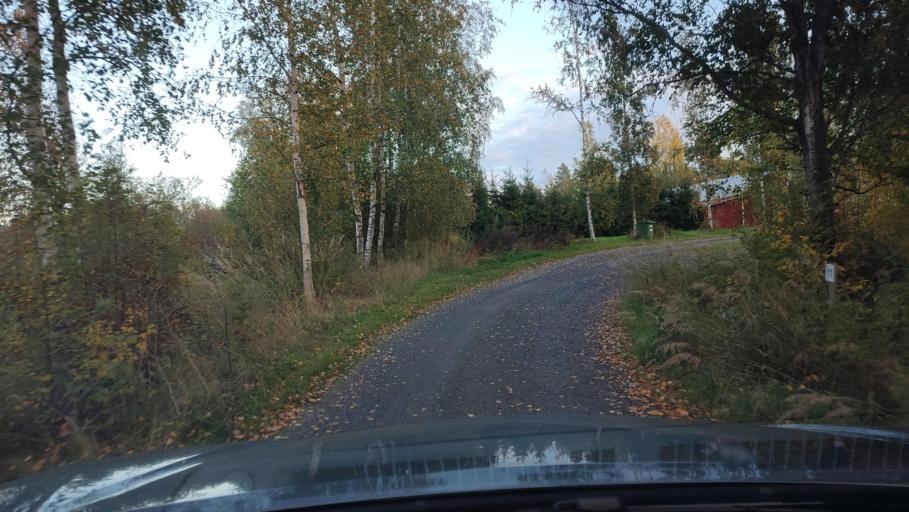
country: FI
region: Ostrobothnia
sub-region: Sydosterbotten
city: Kristinestad
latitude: 62.2419
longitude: 21.5153
